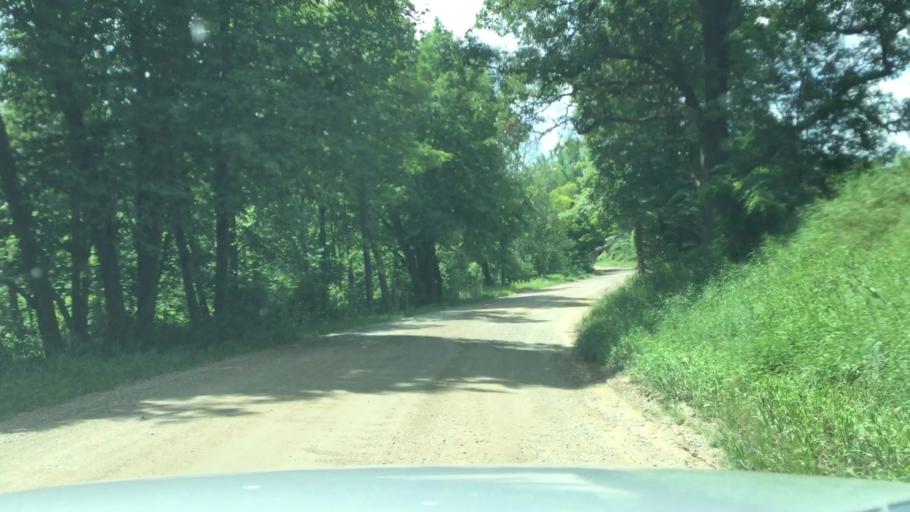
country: US
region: Michigan
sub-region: Ionia County
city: Belding
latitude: 43.1128
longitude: -85.2060
